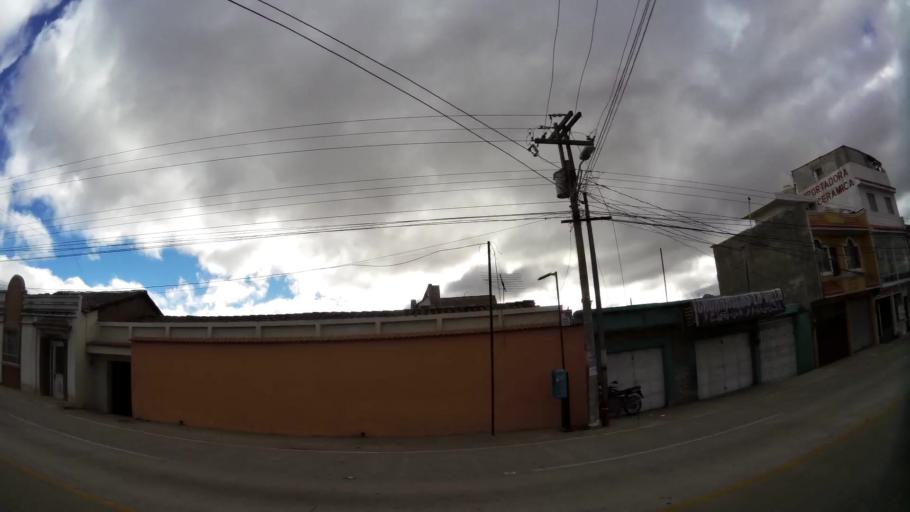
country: GT
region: Quetzaltenango
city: Salcaja
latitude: 14.8729
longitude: -91.4646
